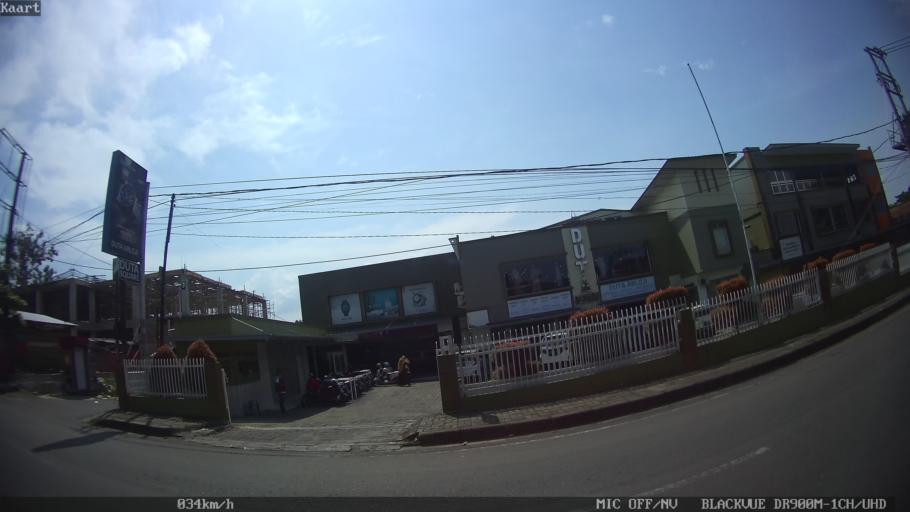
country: ID
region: Lampung
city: Bandarlampung
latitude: -5.4067
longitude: 105.2581
